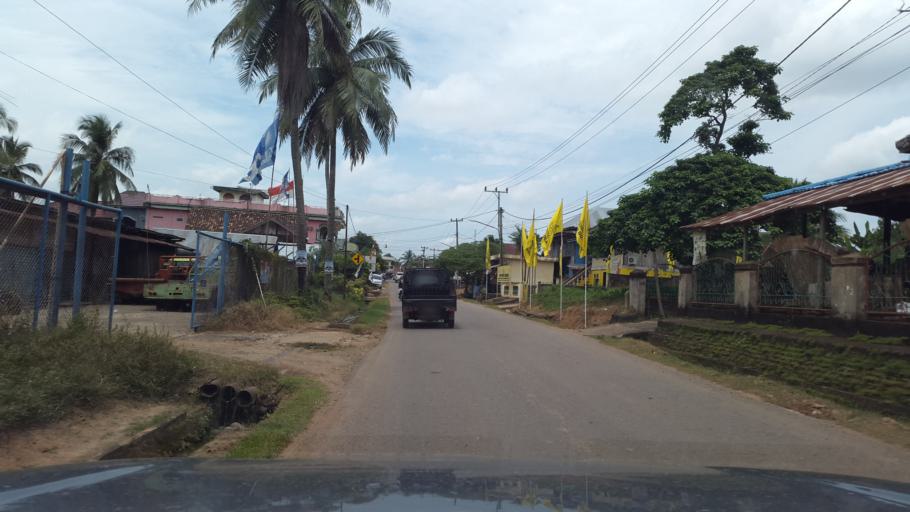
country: ID
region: South Sumatra
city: Gunungmegang Dalam
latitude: -3.2840
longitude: 103.8344
